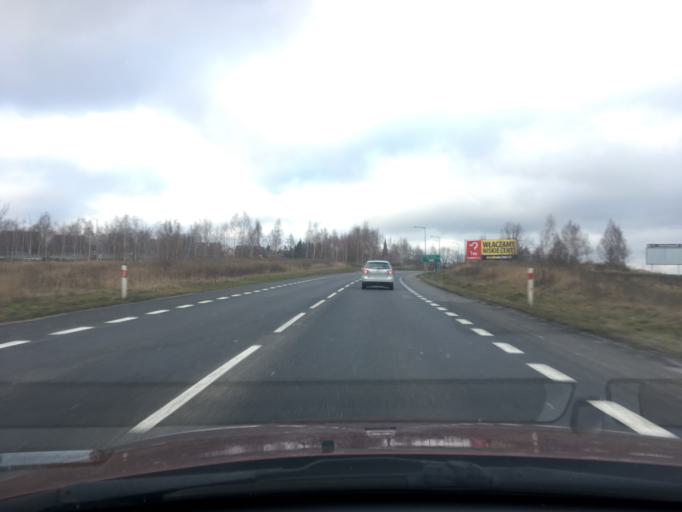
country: PL
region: Lower Silesian Voivodeship
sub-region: Powiat zgorzelecki
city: Lagow
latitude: 51.1478
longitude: 15.0311
